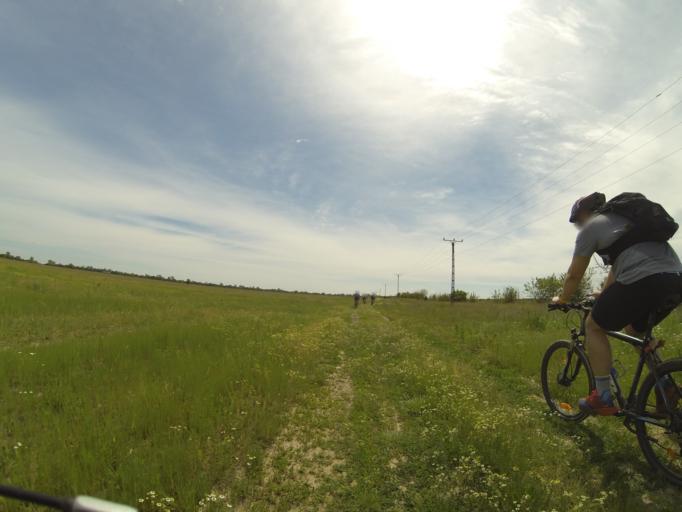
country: RO
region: Dolj
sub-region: Comuna Leu
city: Leu
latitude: 44.2029
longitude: 23.9704
